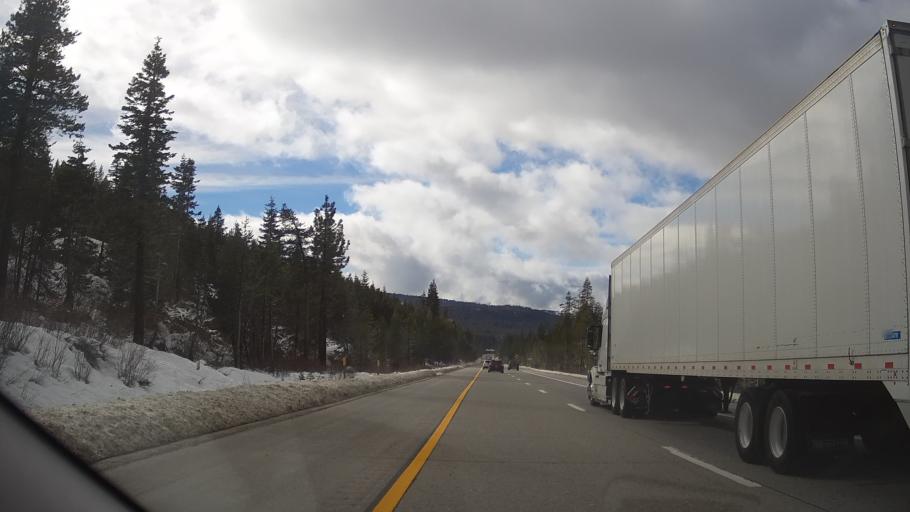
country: US
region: California
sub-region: Nevada County
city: Truckee
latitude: 39.3239
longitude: -120.4167
